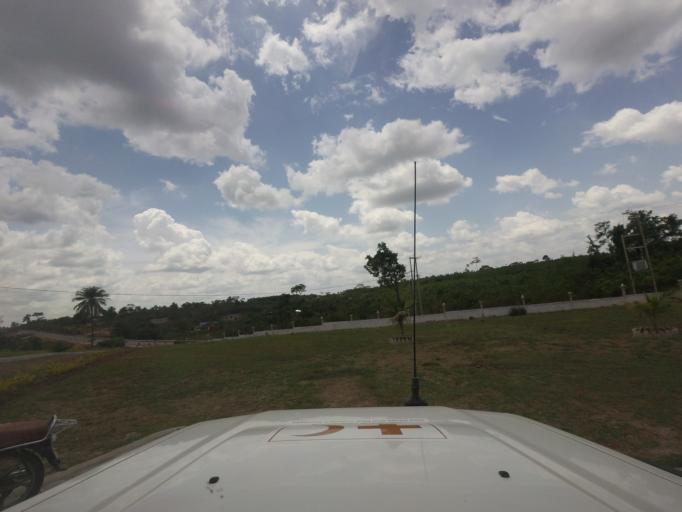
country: LR
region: Nimba
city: Sanniquellie
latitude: 7.2188
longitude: -9.0068
